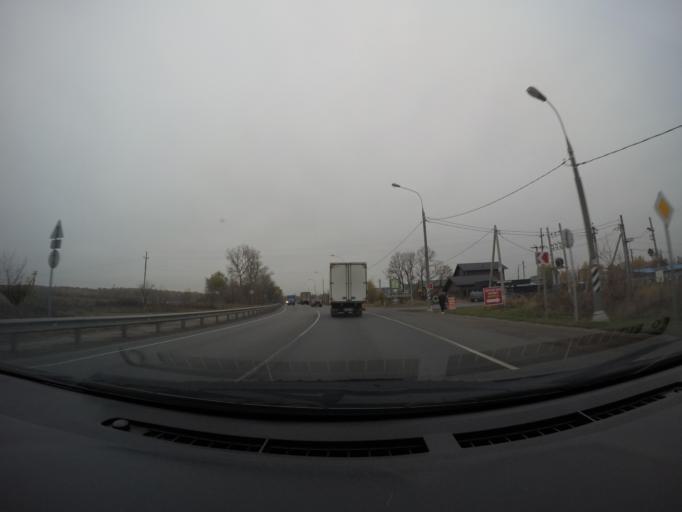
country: RU
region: Moskovskaya
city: Bronnitsy
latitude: 55.3870
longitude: 38.1934
